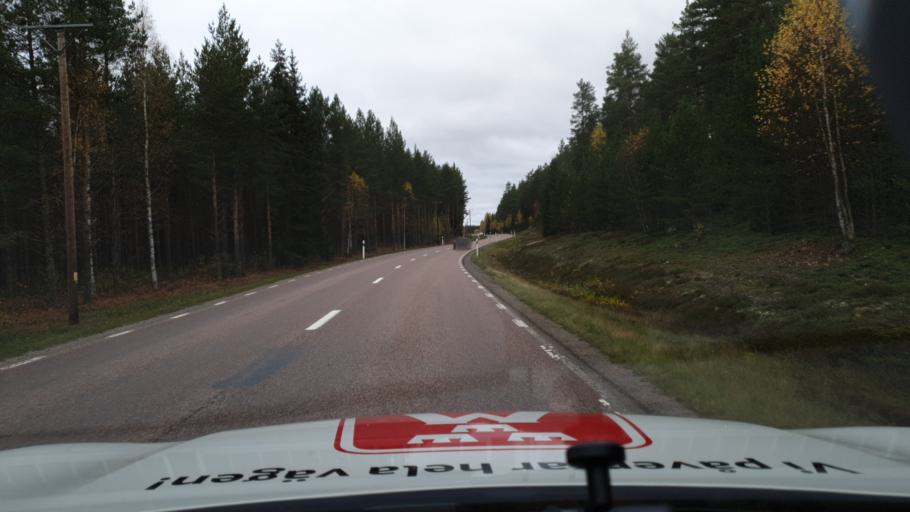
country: SE
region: Gaevleborg
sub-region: Gavle Kommun
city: Hedesunda
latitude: 60.4752
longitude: 16.9411
